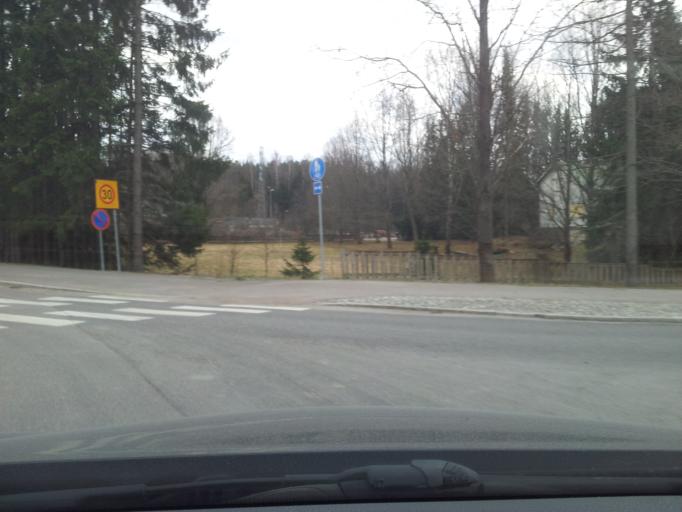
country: FI
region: Uusimaa
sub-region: Helsinki
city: Kilo
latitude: 60.2095
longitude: 24.7954
